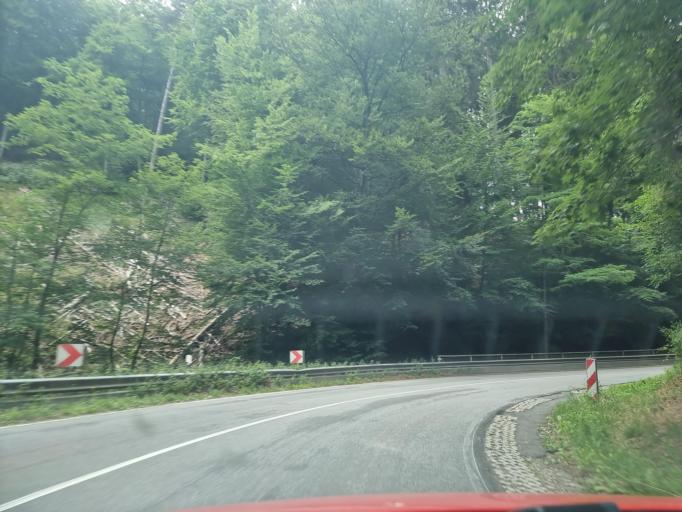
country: DE
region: Rheinland-Pfalz
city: Zemmer
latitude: 49.8517
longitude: 6.6966
